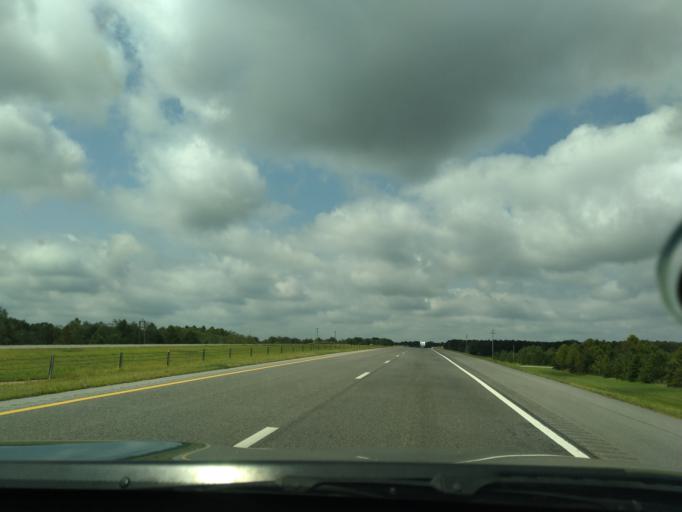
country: US
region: North Carolina
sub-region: Martin County
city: Robersonville
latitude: 35.8375
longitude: -77.2493
